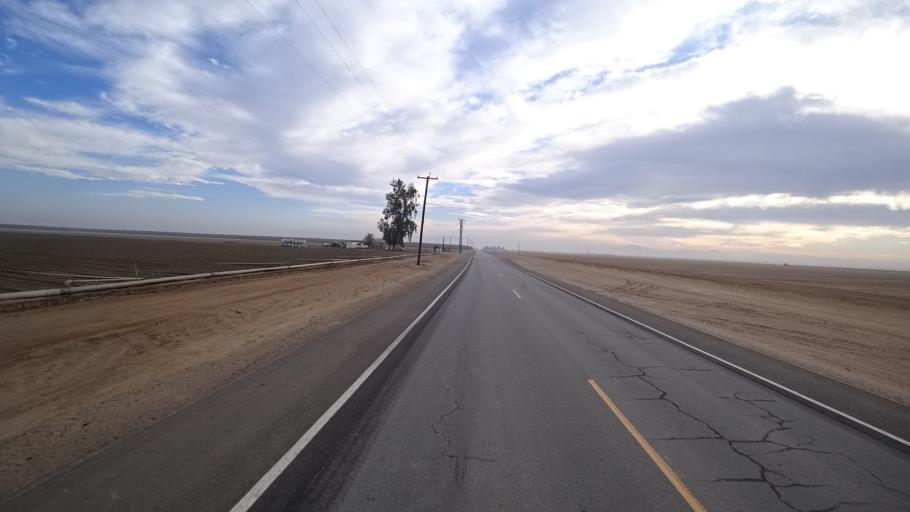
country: US
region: California
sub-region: Kern County
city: Rosedale
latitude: 35.4198
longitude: -119.2181
